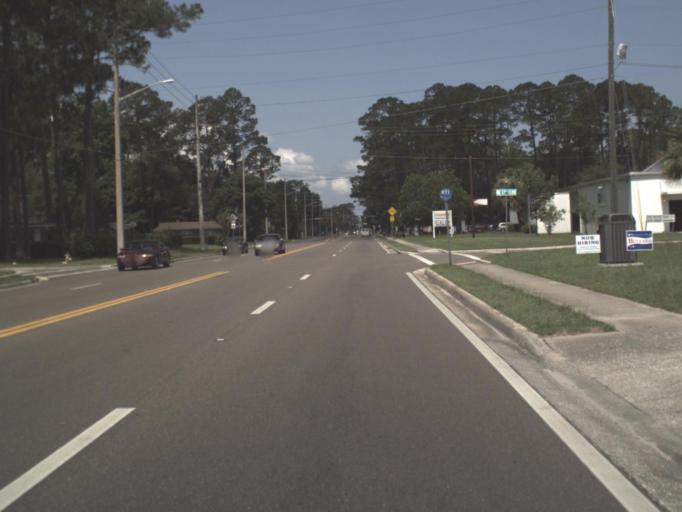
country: US
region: Florida
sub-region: Alachua County
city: Gainesville
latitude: 29.6739
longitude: -82.3026
